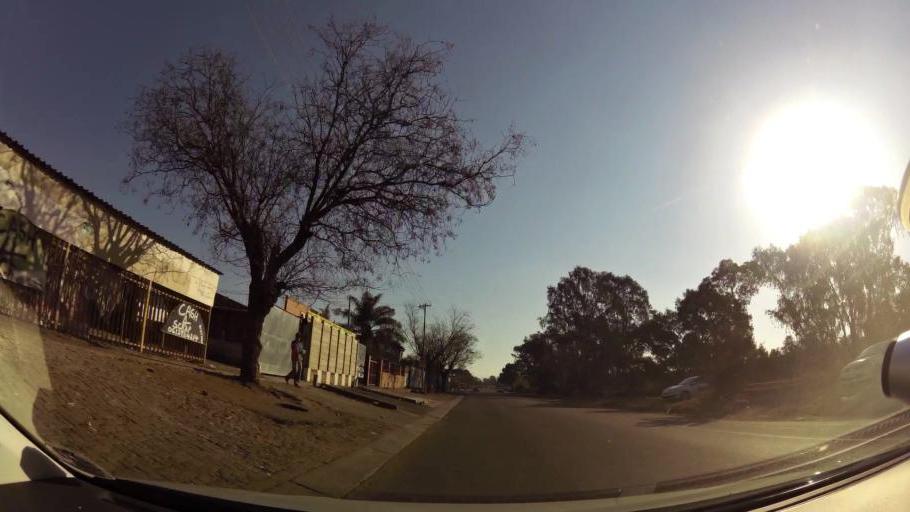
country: ZA
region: Gauteng
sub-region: City of Tshwane Metropolitan Municipality
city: Pretoria
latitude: -25.7437
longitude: 28.1586
